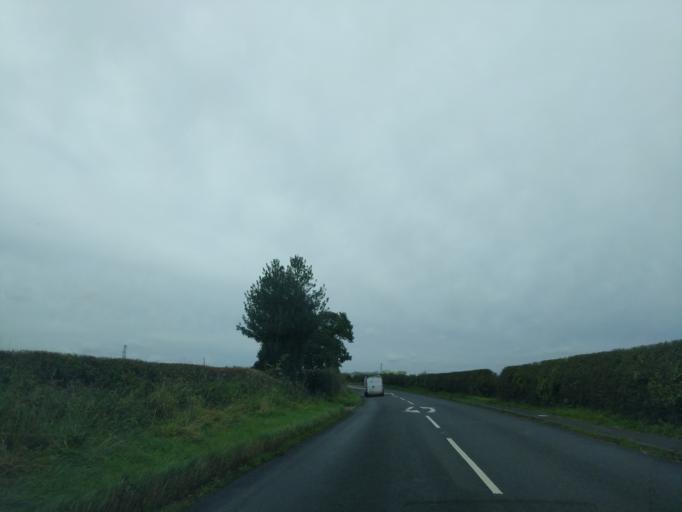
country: GB
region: England
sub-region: Cheshire East
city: Chorlton
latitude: 53.0150
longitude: -2.3578
